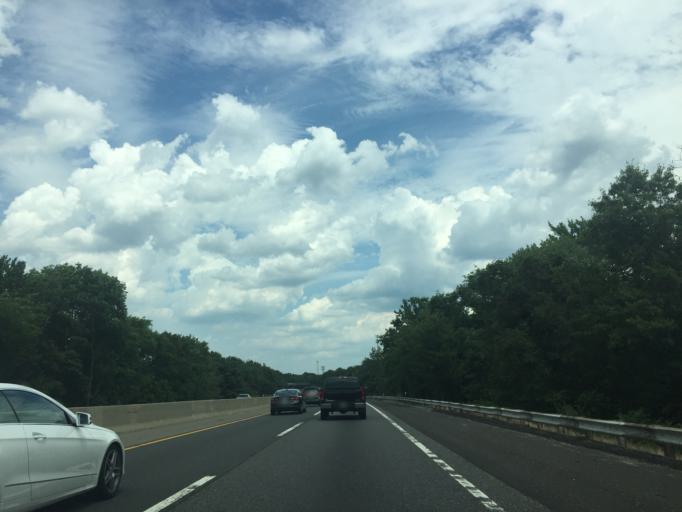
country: US
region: New Jersey
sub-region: Camden County
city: Ashland
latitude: 39.8749
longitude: -75.0142
